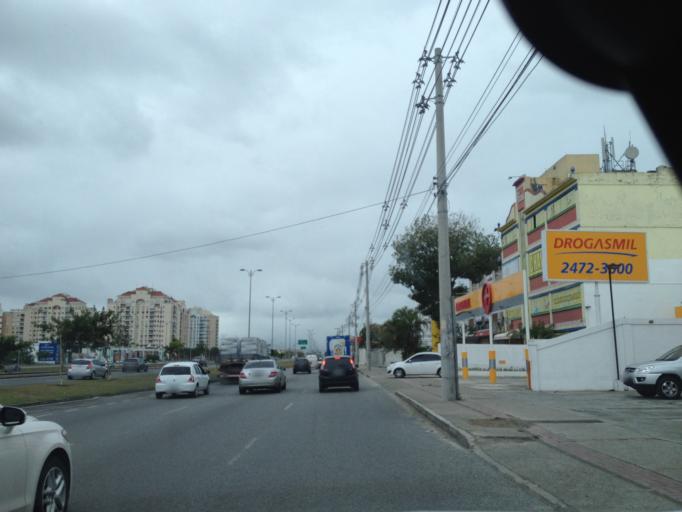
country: BR
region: Rio de Janeiro
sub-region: Nilopolis
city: Nilopolis
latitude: -23.0172
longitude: -43.4762
